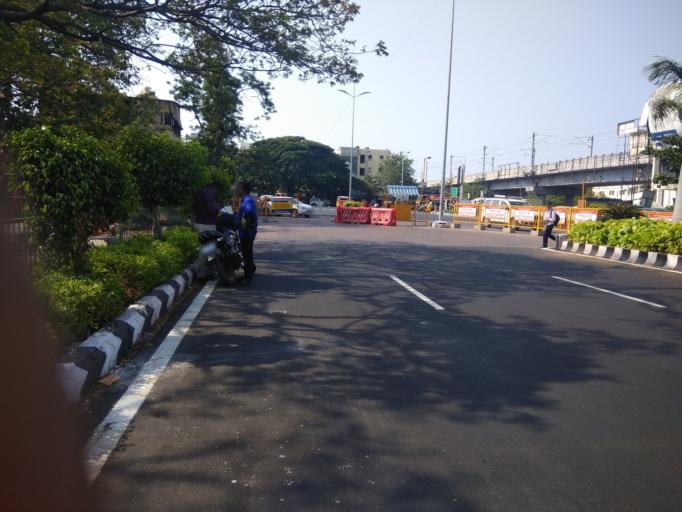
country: IN
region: Tamil Nadu
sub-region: Chennai
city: Gandhi Nagar
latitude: 13.0059
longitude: 80.2473
